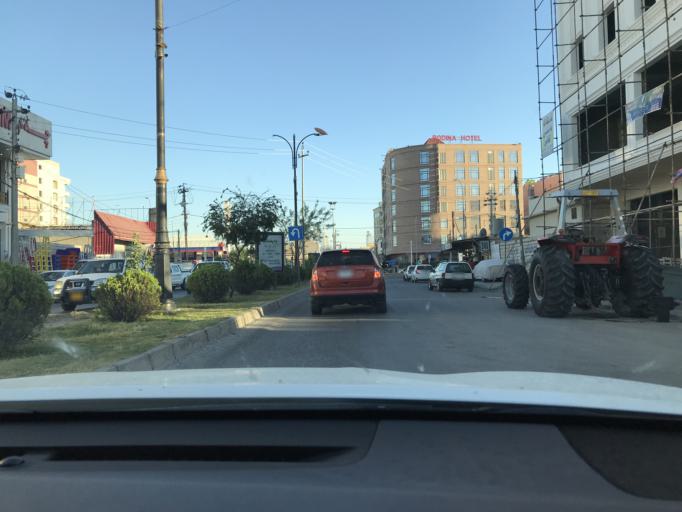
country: IQ
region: Arbil
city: Erbil
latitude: 36.2046
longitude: 44.0099
